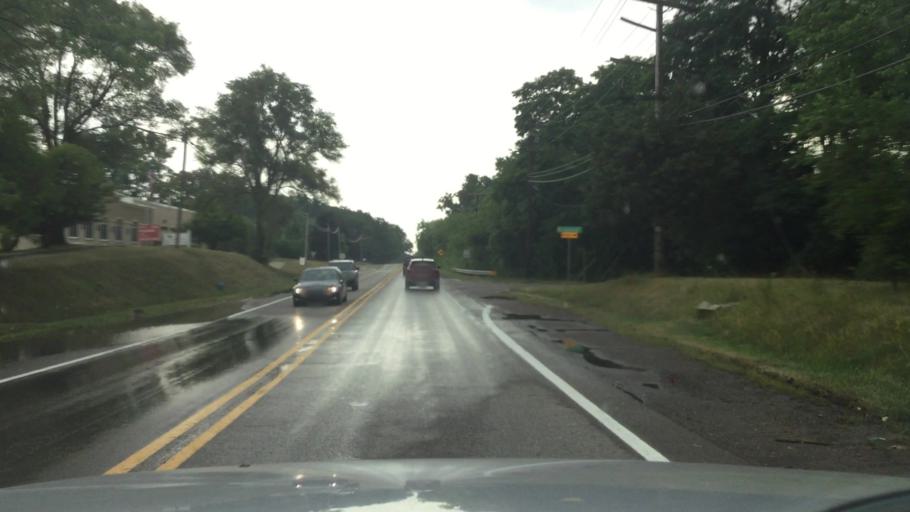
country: US
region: Michigan
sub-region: Oakland County
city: Sylvan Lake
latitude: 42.6732
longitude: -83.3474
